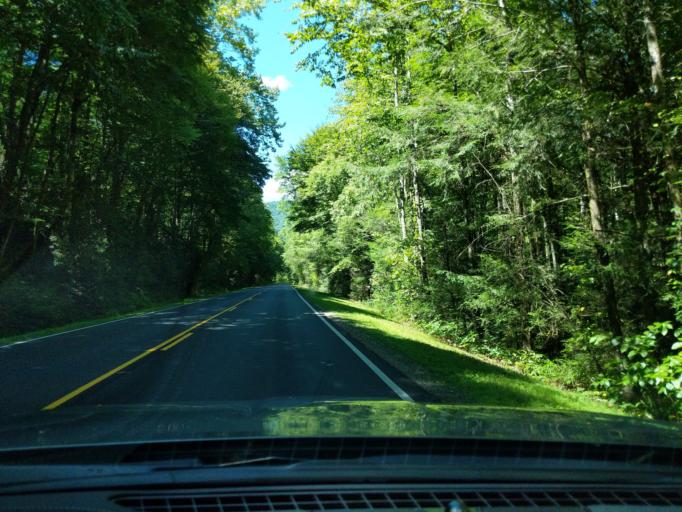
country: US
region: North Carolina
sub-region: Swain County
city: Cherokee
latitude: 35.5705
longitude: -83.3379
